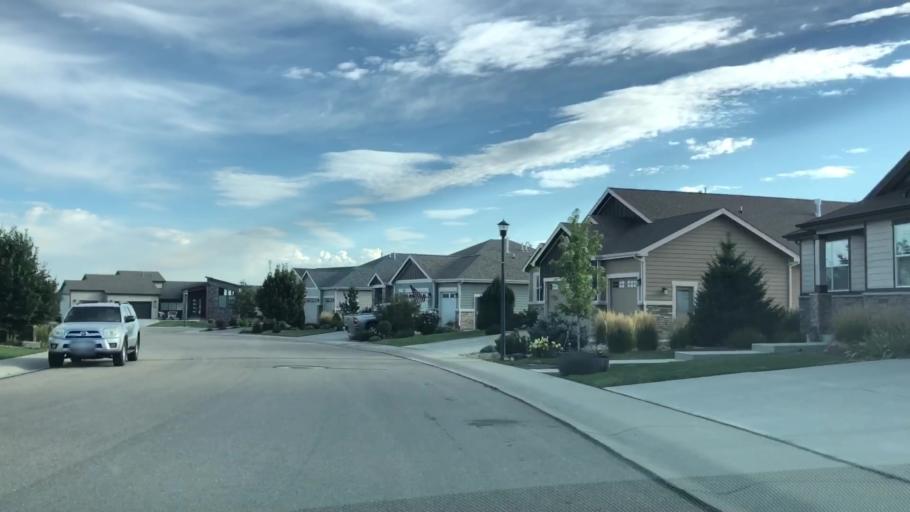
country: US
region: Colorado
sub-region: Weld County
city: Windsor
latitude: 40.4567
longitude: -104.9667
